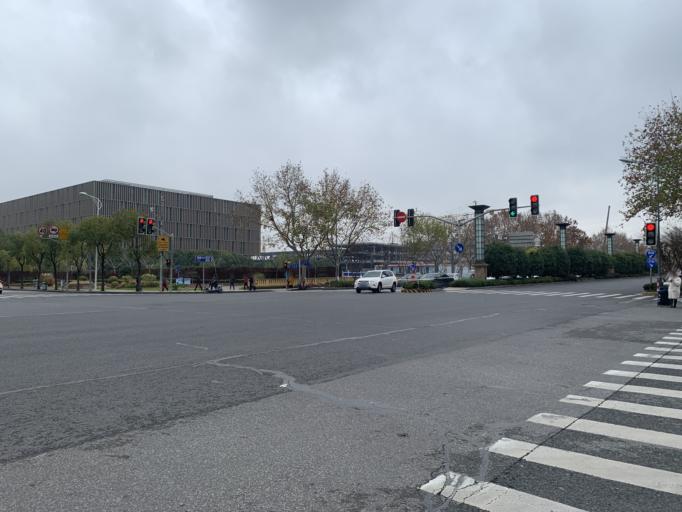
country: CN
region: Shanghai Shi
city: Huamu
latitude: 31.1948
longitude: 121.5345
